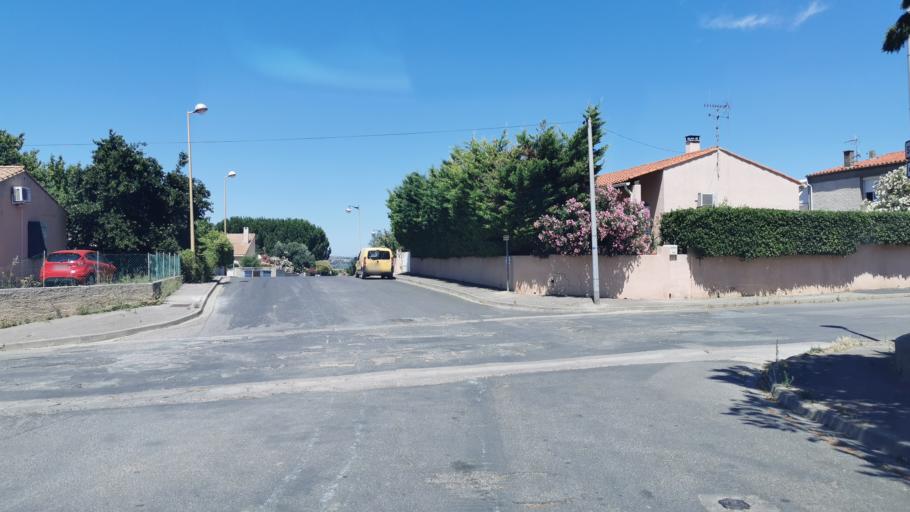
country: FR
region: Languedoc-Roussillon
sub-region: Departement de l'Aude
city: Fleury
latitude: 43.2281
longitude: 3.1389
